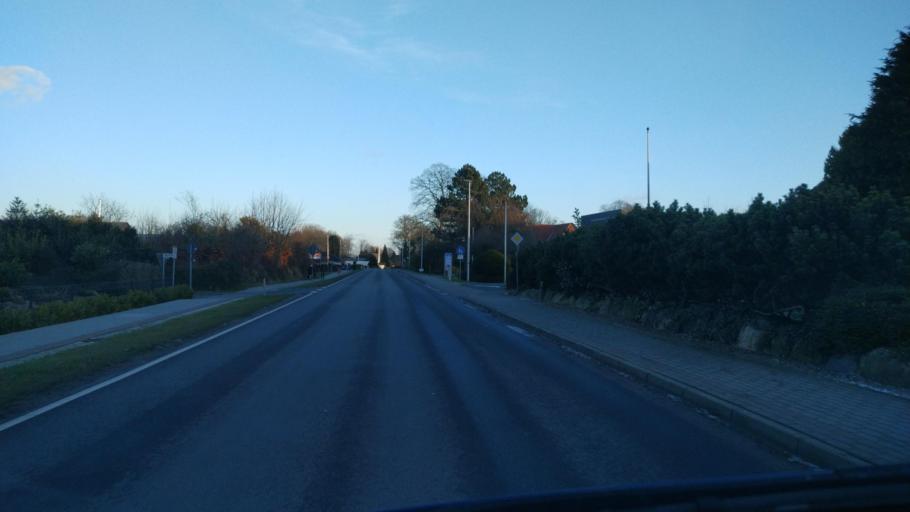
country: DE
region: Schleswig-Holstein
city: Ostenfeld
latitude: 54.4622
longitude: 9.2333
